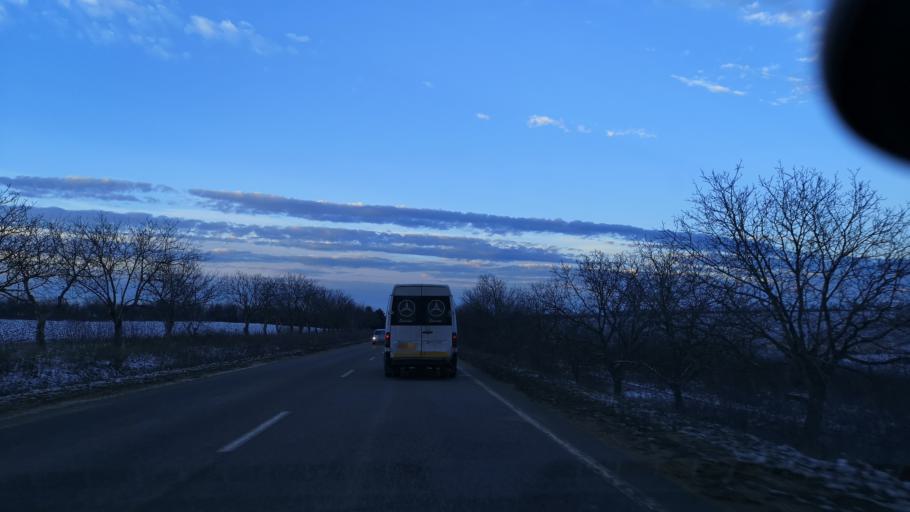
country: MD
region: Orhei
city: Orhei
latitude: 47.5449
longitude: 28.7928
